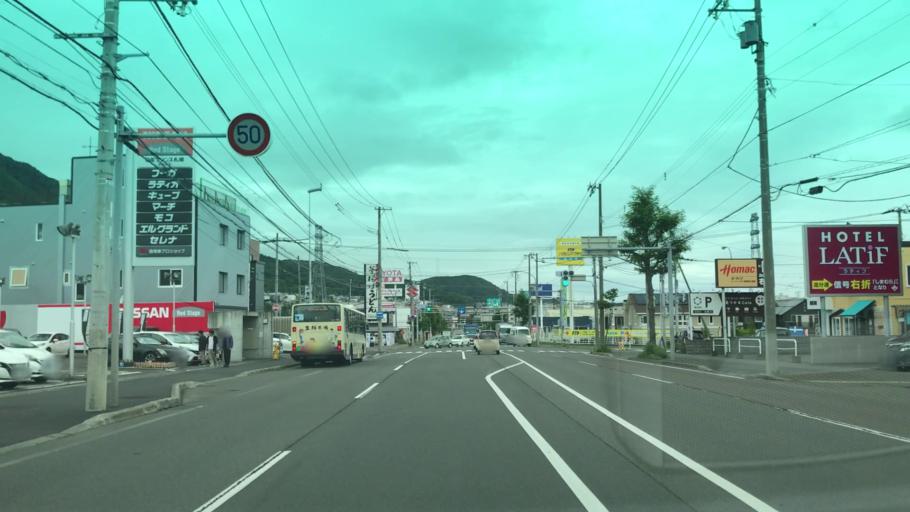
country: JP
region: Hokkaido
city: Sapporo
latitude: 43.0941
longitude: 141.2632
